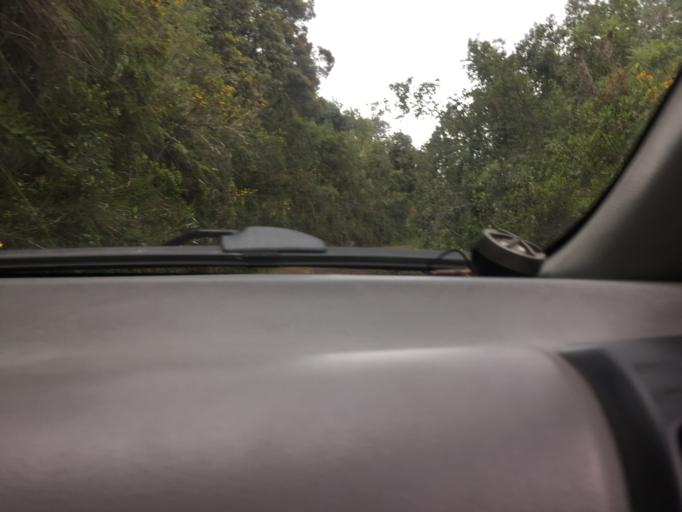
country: EC
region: Imbabura
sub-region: Canton Otavalo
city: Otavalo
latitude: 0.0819
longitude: -78.2982
